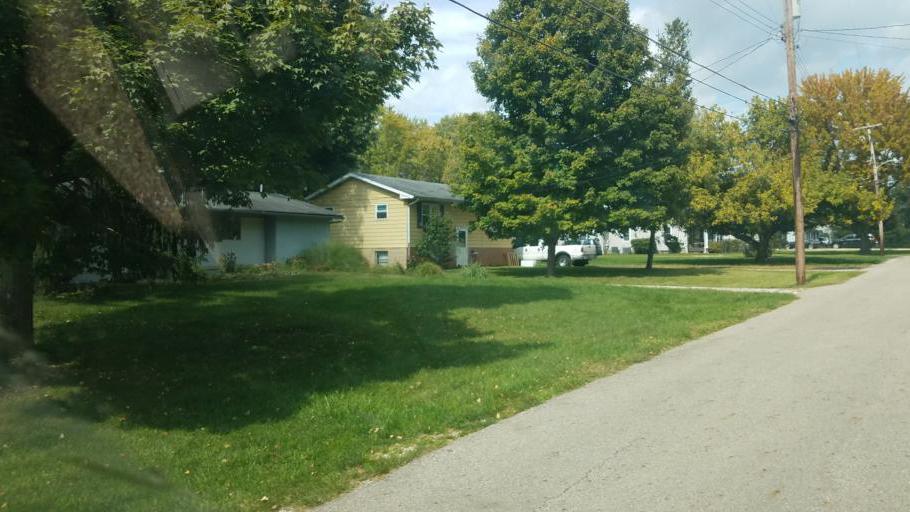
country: US
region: Ohio
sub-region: Franklin County
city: Worthington
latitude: 40.0870
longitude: -83.0115
